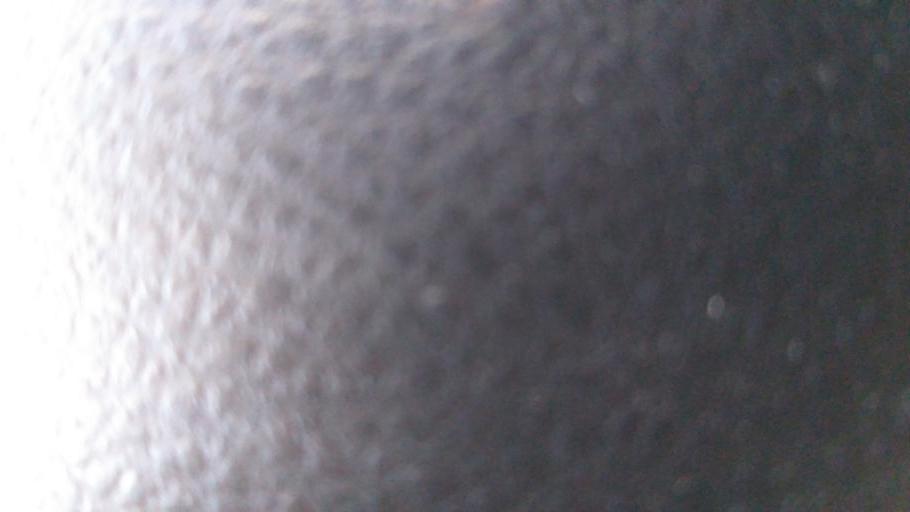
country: SA
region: Makkah
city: Al Hada
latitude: 21.3710
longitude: 40.2641
